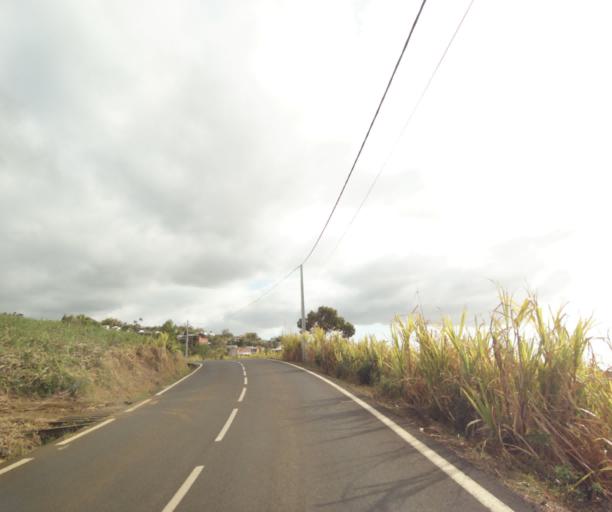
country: RE
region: Reunion
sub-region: Reunion
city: Saint-Paul
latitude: -21.0268
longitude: 55.3122
